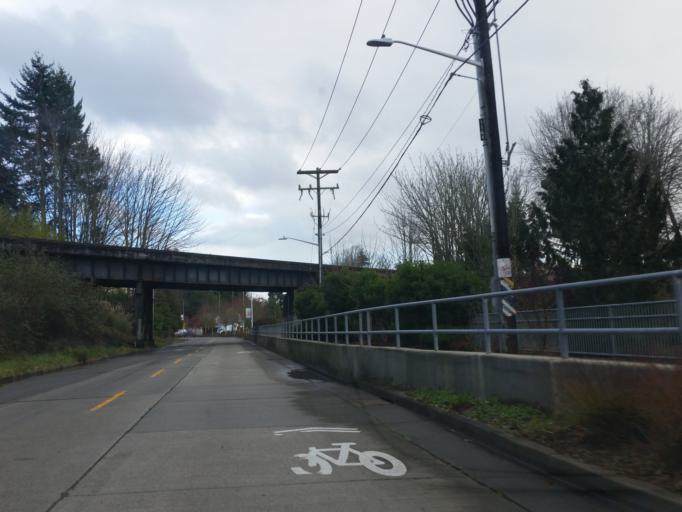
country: US
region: Washington
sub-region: King County
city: Seattle
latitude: 47.6687
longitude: -122.4029
